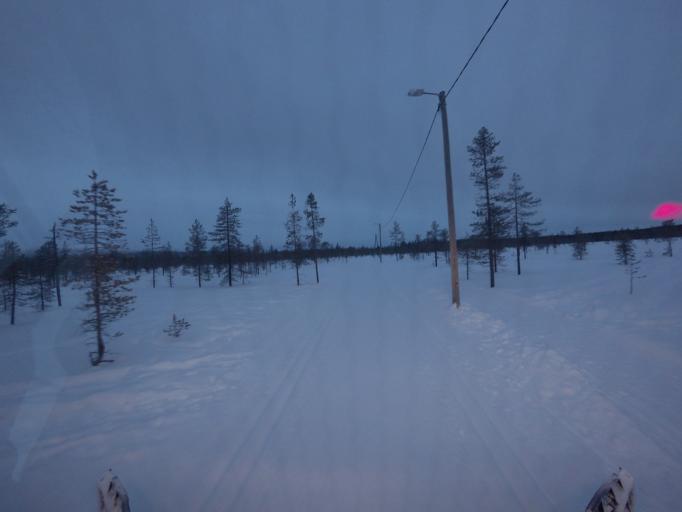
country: FI
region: Lapland
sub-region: Tunturi-Lappi
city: Kolari
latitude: 67.6101
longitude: 24.1728
